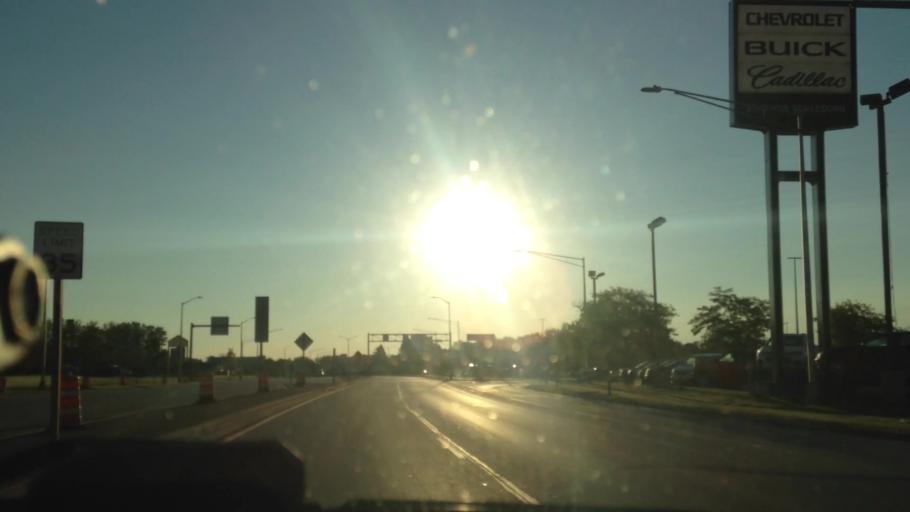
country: US
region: Wisconsin
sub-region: Ozaukee County
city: Saukville
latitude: 43.3850
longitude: -87.9265
